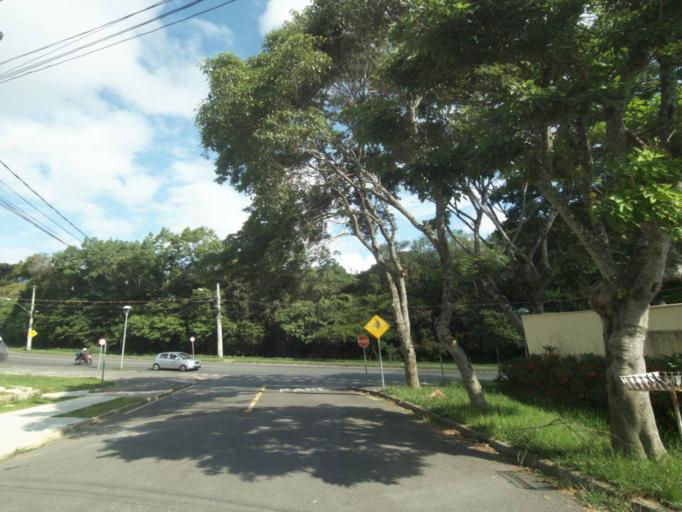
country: BR
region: Parana
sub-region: Curitiba
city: Curitiba
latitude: -25.3842
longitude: -49.2970
